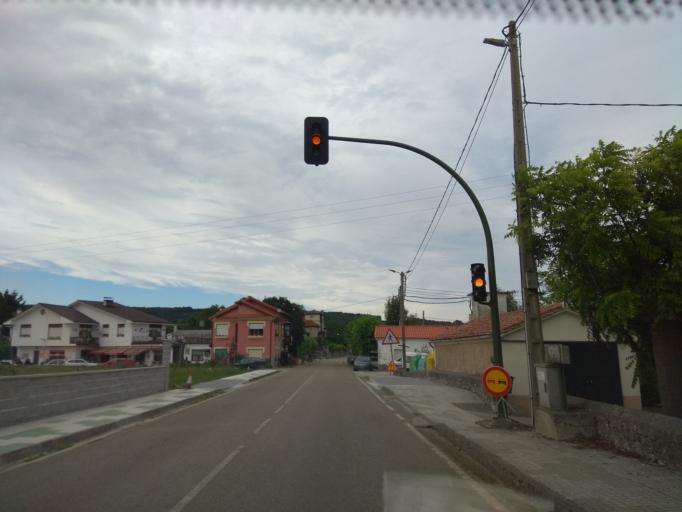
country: ES
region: Cantabria
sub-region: Provincia de Cantabria
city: Hazas de Cesto
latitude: 43.3942
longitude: -3.5889
